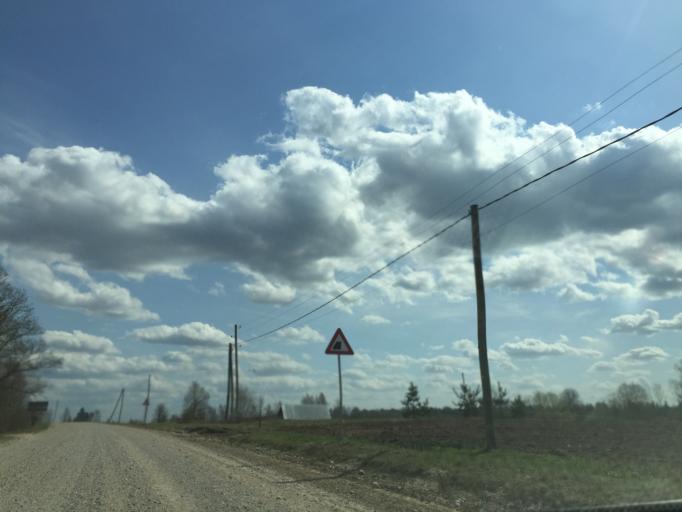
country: LV
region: Skriveri
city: Skriveri
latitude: 56.7463
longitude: 25.0958
